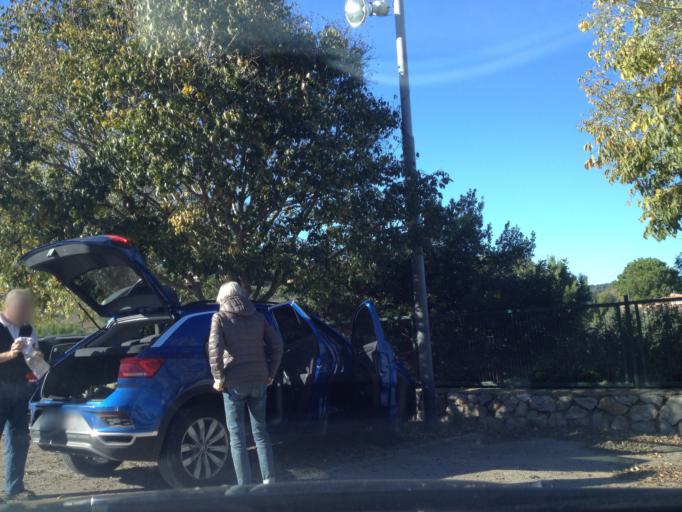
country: ES
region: Balearic Islands
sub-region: Illes Balears
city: Arta
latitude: 39.6972
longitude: 3.3522
